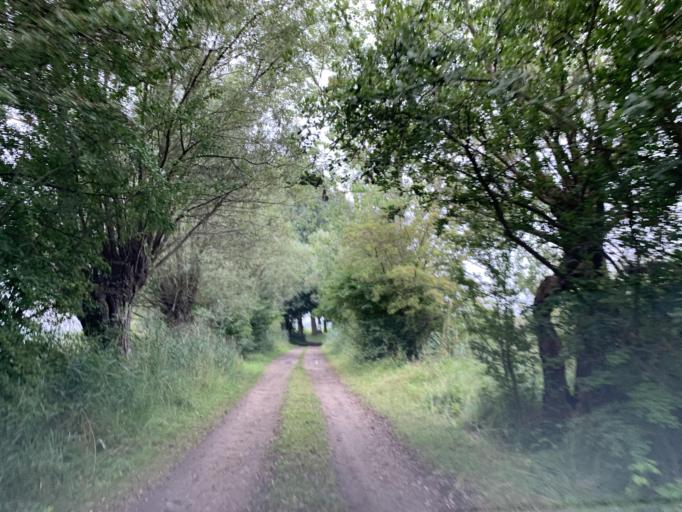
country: DE
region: Mecklenburg-Vorpommern
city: Carpin
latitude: 53.3899
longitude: 13.2332
